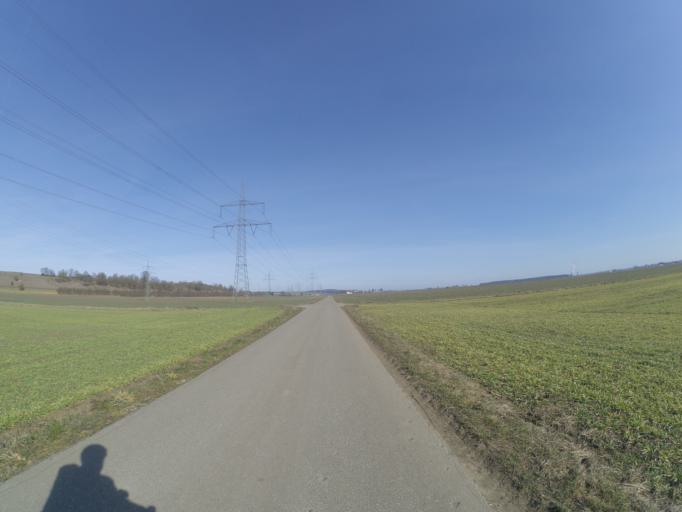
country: DE
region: Baden-Wuerttemberg
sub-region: Regierungsbezirk Stuttgart
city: Niederstotzingen
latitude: 48.5182
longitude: 10.2214
